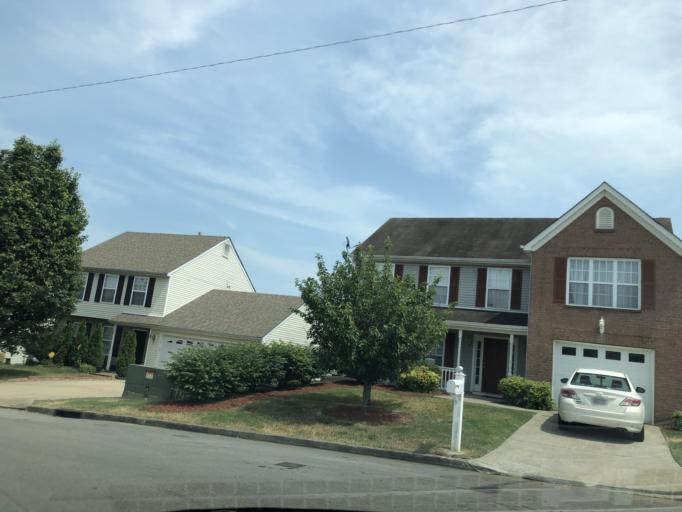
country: US
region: Tennessee
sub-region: Rutherford County
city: La Vergne
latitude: 36.0480
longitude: -86.6165
